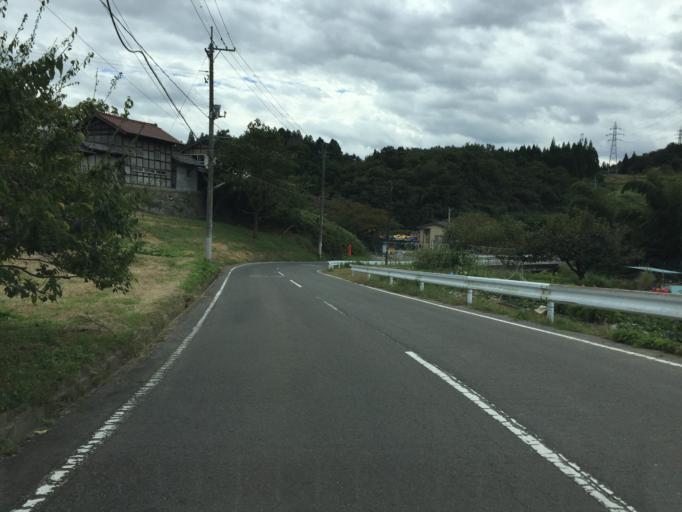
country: JP
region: Fukushima
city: Fukushima-shi
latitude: 37.6925
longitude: 140.4917
